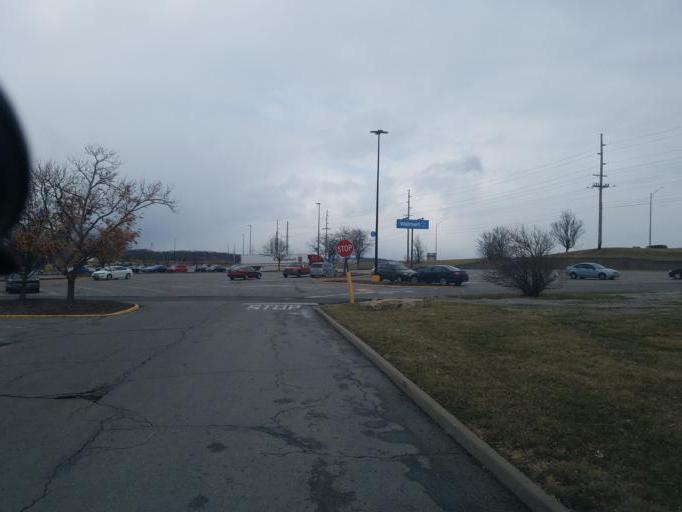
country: US
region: Missouri
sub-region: Boone County
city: Columbia
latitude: 38.9540
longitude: -92.2946
